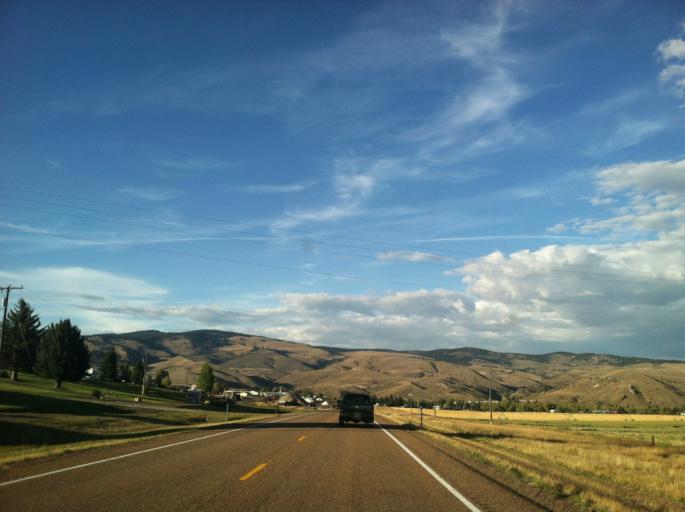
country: US
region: Montana
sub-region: Granite County
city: Philipsburg
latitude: 46.6510
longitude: -113.1617
